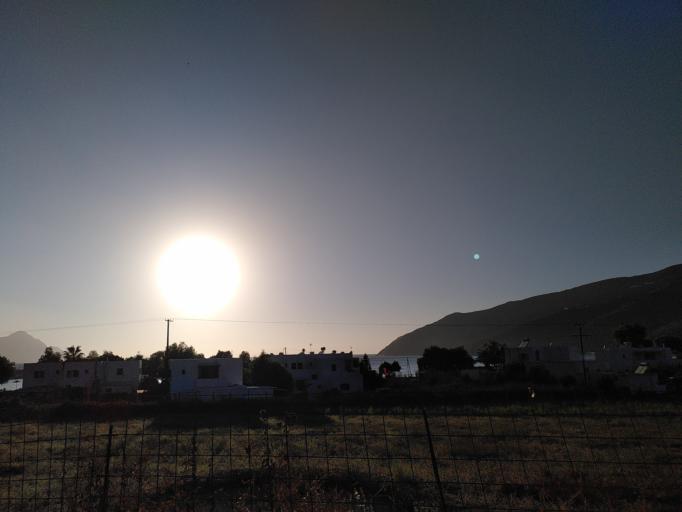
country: GR
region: South Aegean
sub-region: Nomos Kykladon
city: Amorgos
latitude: 36.9025
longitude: 25.9796
